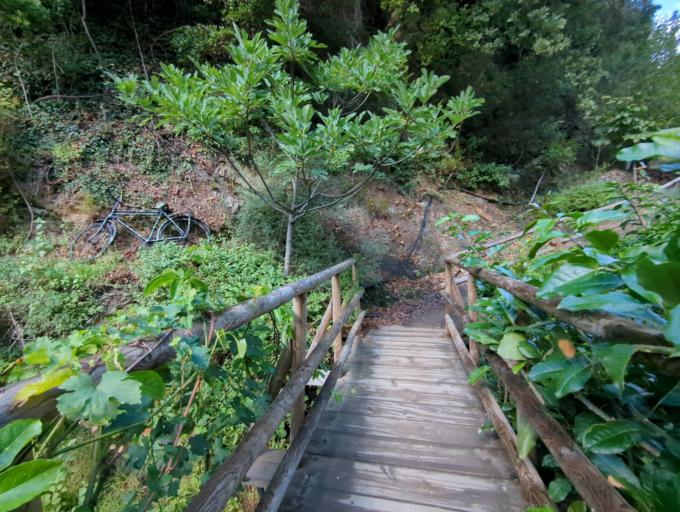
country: GR
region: Crete
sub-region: Nomos Chanias
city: Galatas
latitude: 35.4174
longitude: 23.9388
